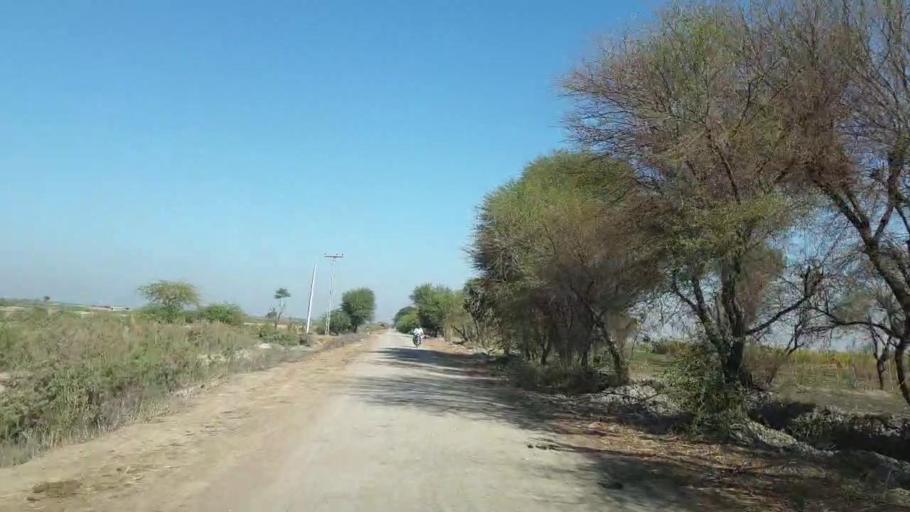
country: PK
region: Sindh
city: Mirpur Khas
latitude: 25.6160
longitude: 69.0240
